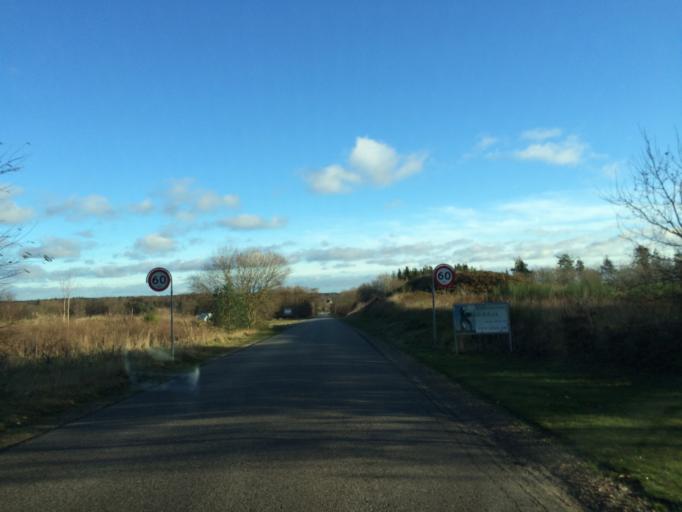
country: DK
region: Central Jutland
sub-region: Herning Kommune
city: Kibaek
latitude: 56.0384
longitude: 8.8447
